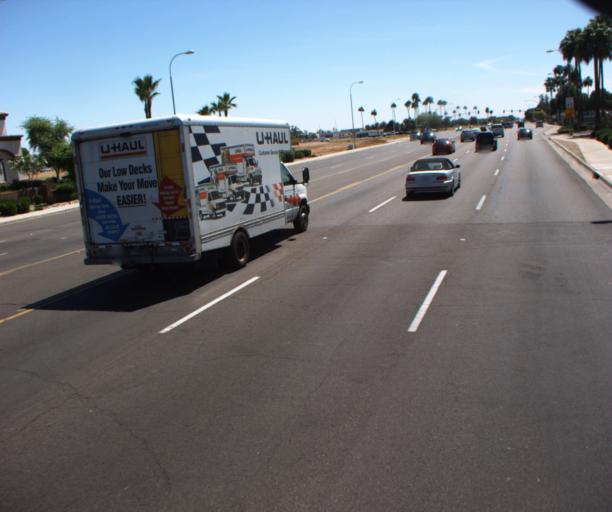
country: US
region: Arizona
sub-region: Maricopa County
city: San Carlos
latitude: 33.3522
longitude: -111.8419
